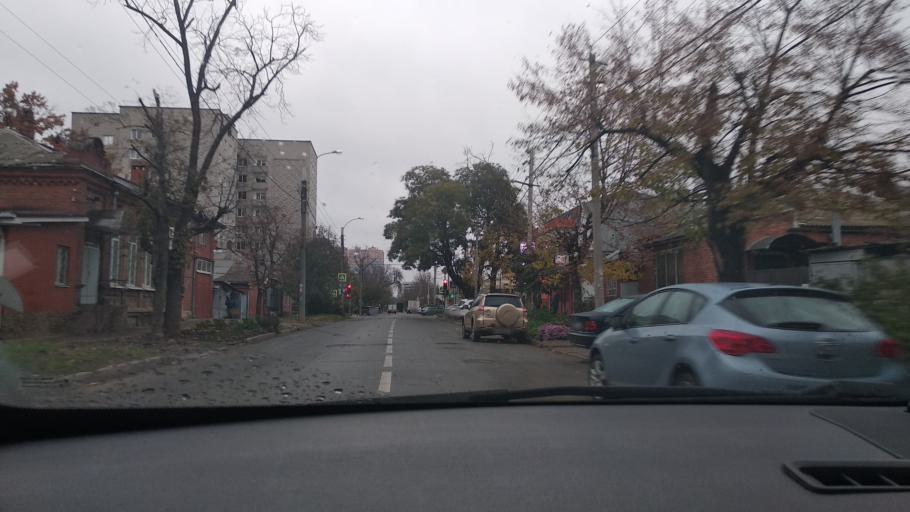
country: RU
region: Krasnodarskiy
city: Krasnodar
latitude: 45.0319
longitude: 38.9842
